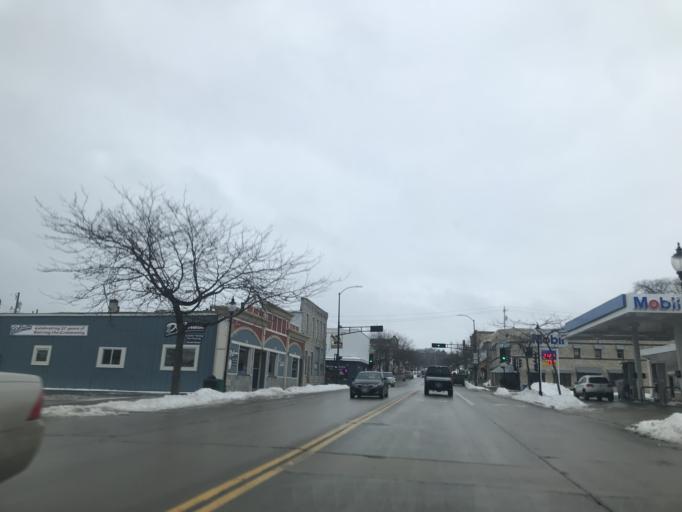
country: US
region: Wisconsin
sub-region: Door County
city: Sturgeon Bay
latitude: 44.8296
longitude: -87.3845
